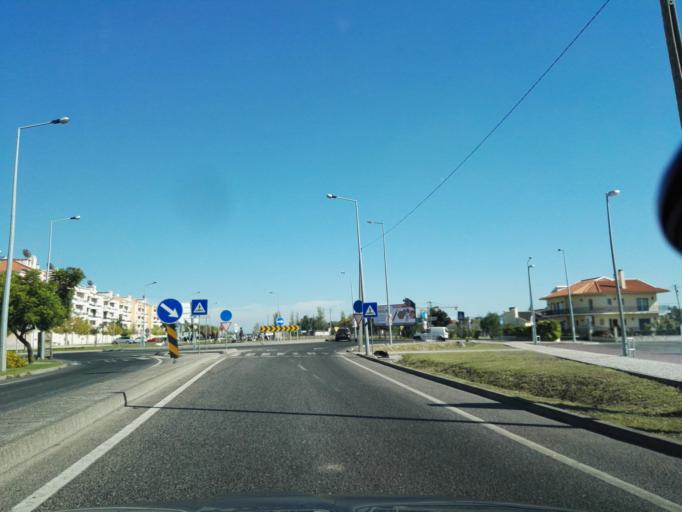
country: PT
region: Santarem
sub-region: Benavente
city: Samora Correia
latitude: 38.9204
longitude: -8.8780
